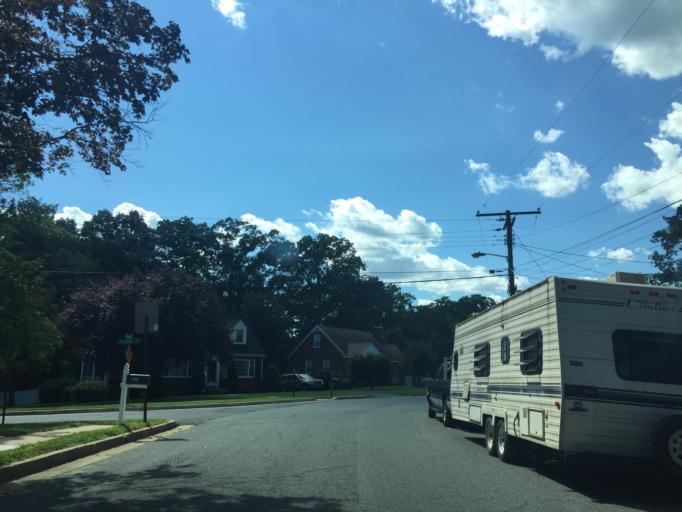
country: US
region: Maryland
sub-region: Baltimore County
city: Perry Hall
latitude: 39.4041
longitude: -76.4702
